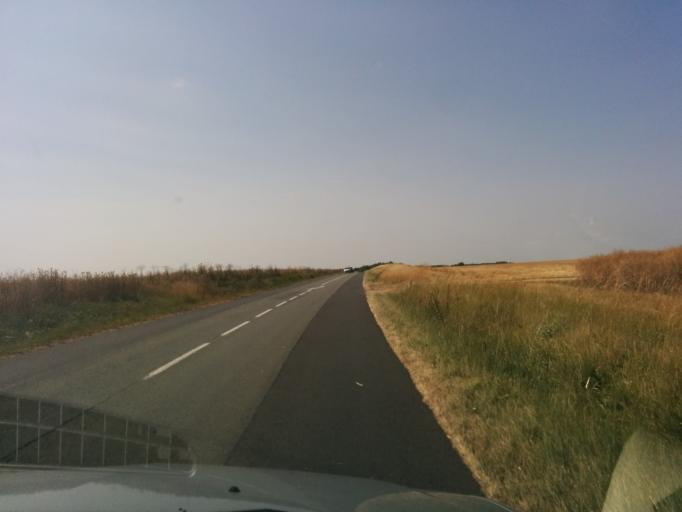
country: FR
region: Poitou-Charentes
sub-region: Departement de la Vienne
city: Mirebeau
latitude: 46.7742
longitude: 0.1417
